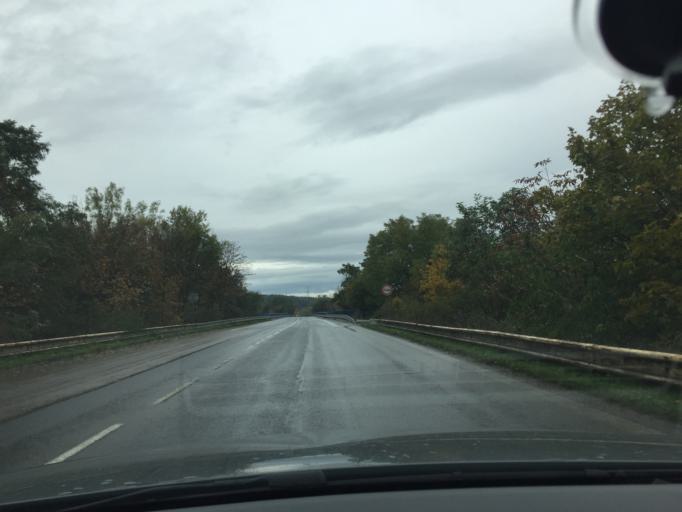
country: CZ
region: Central Bohemia
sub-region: Okres Melnik
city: Veltrusy
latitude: 50.2780
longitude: 14.3177
